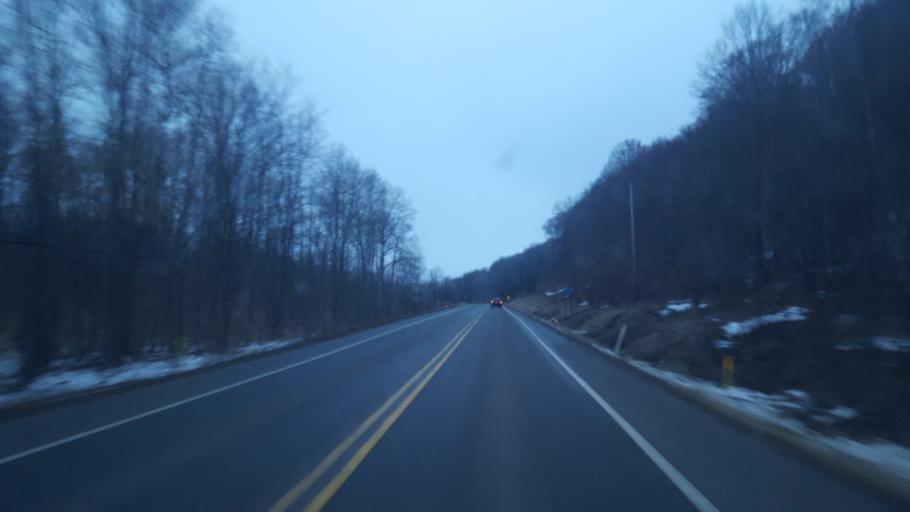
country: US
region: Pennsylvania
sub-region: Potter County
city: Coudersport
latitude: 41.7491
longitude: -78.0961
